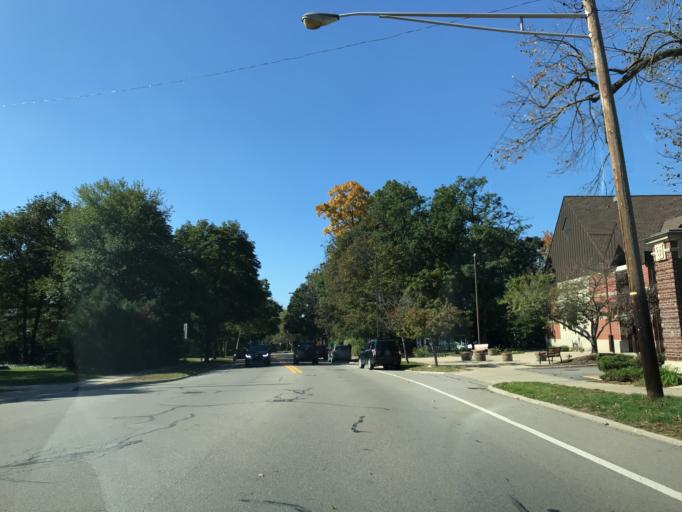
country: US
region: Michigan
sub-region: Washtenaw County
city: Ann Arbor
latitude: 42.2724
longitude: -83.7296
